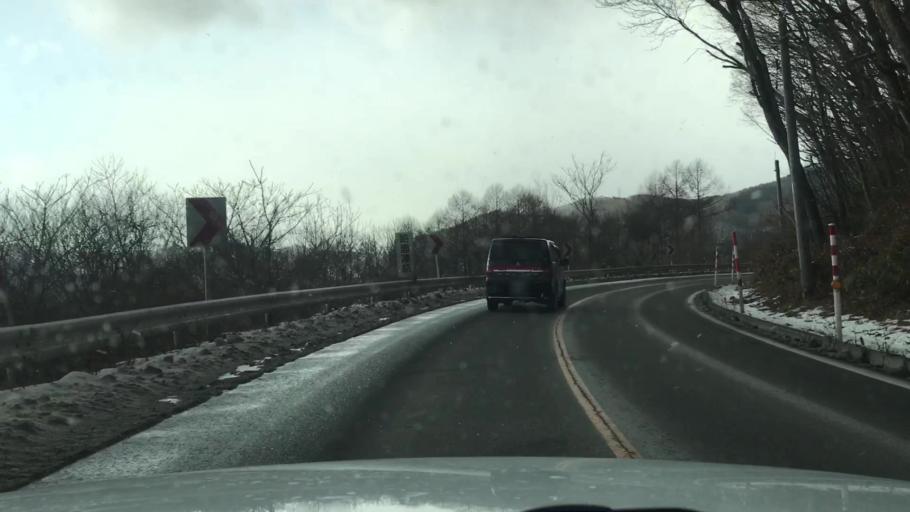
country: JP
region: Iwate
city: Morioka-shi
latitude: 39.6628
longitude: 141.3276
